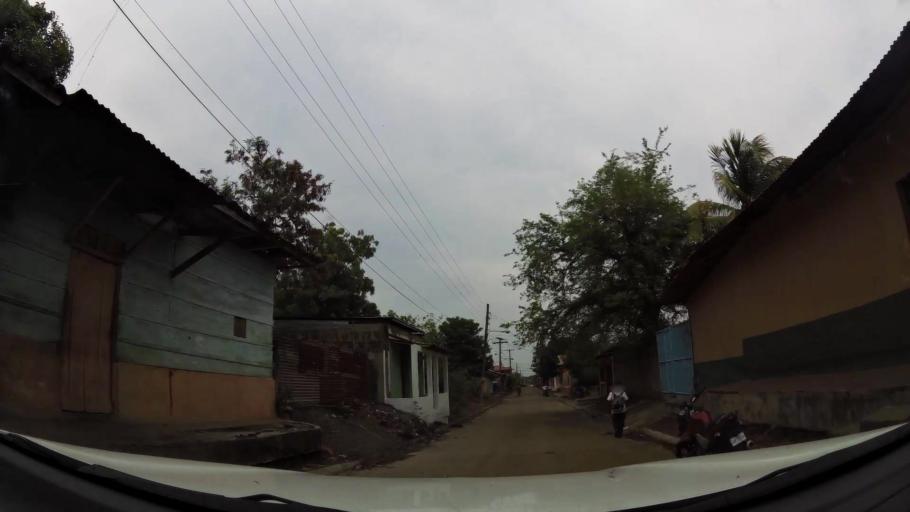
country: NI
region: Granada
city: Nandaime
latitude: 11.7592
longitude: -86.0552
